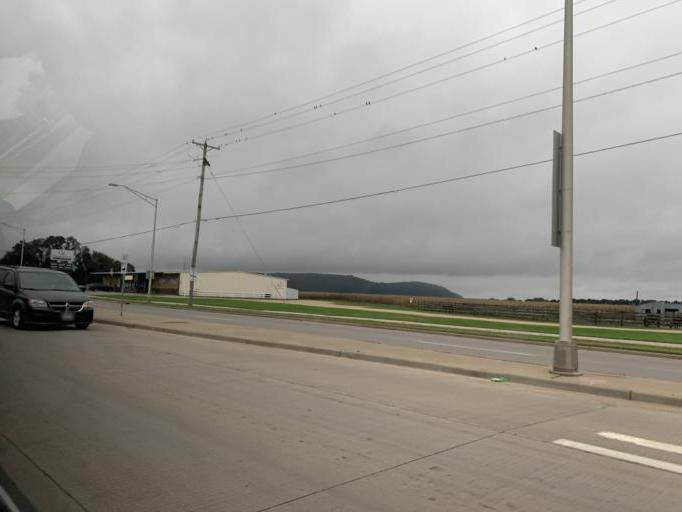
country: US
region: Wisconsin
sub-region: Crawford County
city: Prairie du Chien
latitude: 43.0263
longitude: -91.1244
